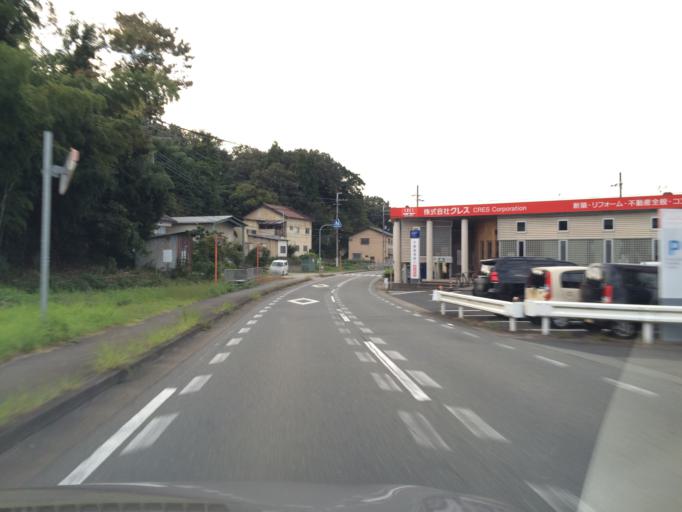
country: JP
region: Hyogo
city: Toyooka
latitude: 35.5230
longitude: 134.8187
